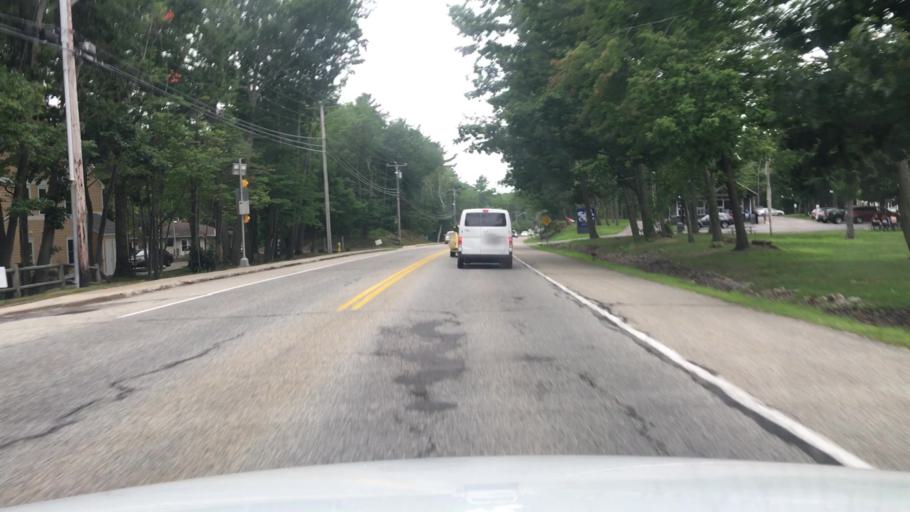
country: US
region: Maine
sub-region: York County
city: Old Orchard Beach
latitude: 43.5124
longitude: -70.3924
